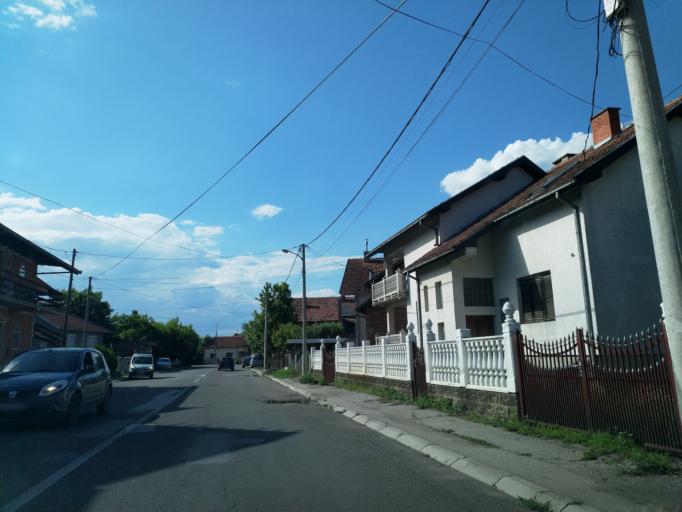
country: RS
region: Central Serbia
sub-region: Pomoravski Okrug
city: Paracin
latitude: 43.8606
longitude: 21.4037
